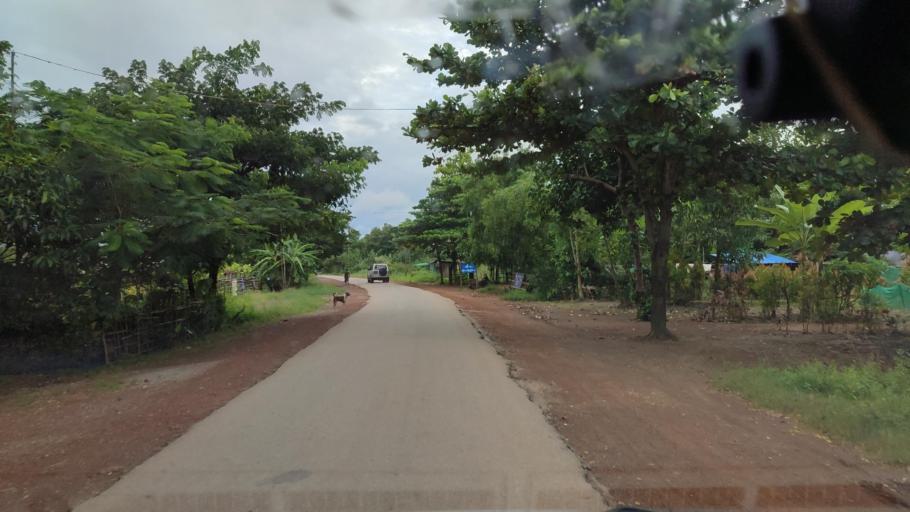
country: MM
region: Bago
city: Nyaunglebin
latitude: 17.9436
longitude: 96.8078
